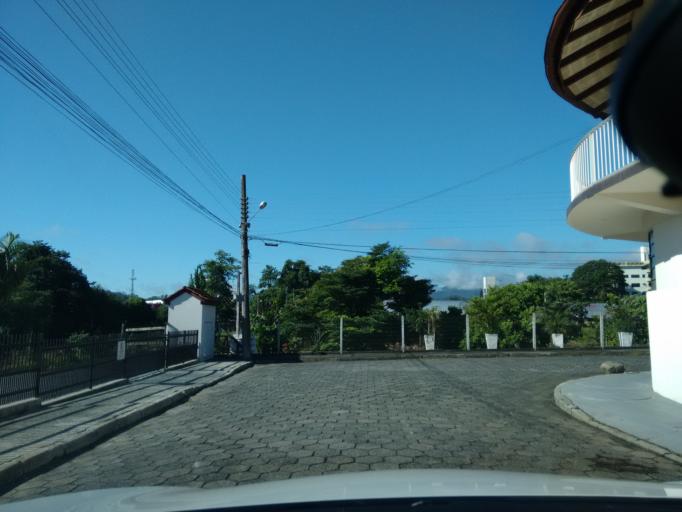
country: BR
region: Santa Catarina
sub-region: Pomerode
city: Pomerode
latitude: -26.7314
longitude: -49.1759
